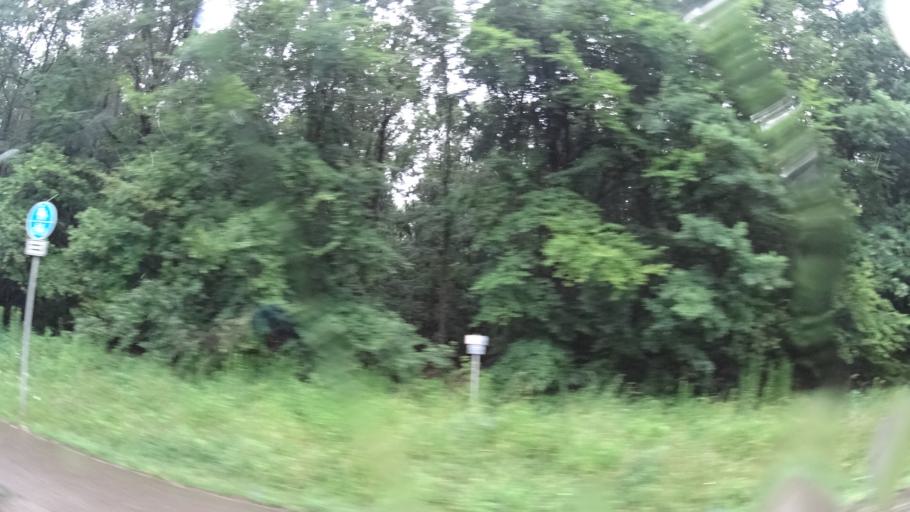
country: DE
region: Saarland
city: Friedrichsthal
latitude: 49.3322
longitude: 7.0798
